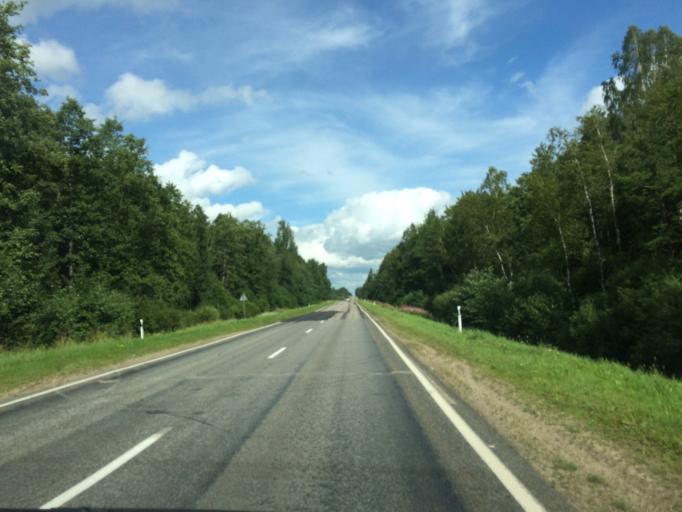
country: LV
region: Rezekne
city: Rezekne
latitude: 56.6434
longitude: 27.4854
